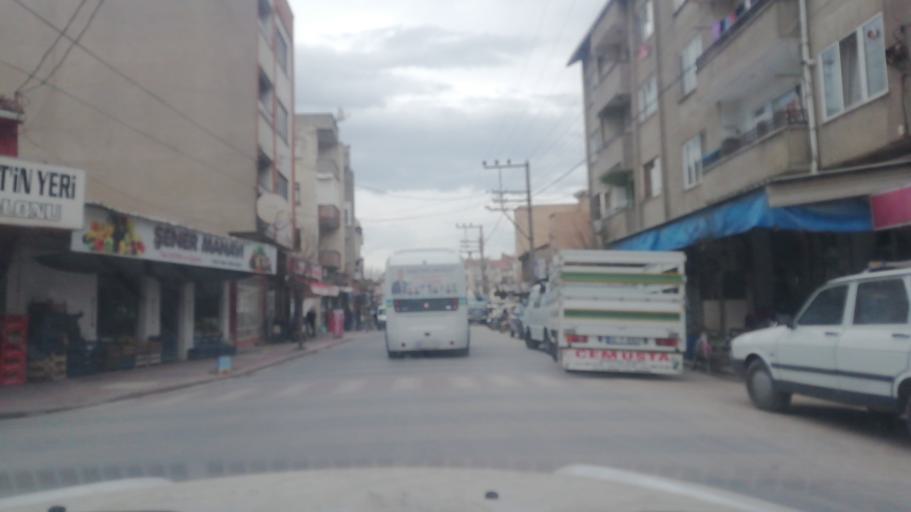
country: TR
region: Balikesir
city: Gonen
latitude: 40.1010
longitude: 27.6505
